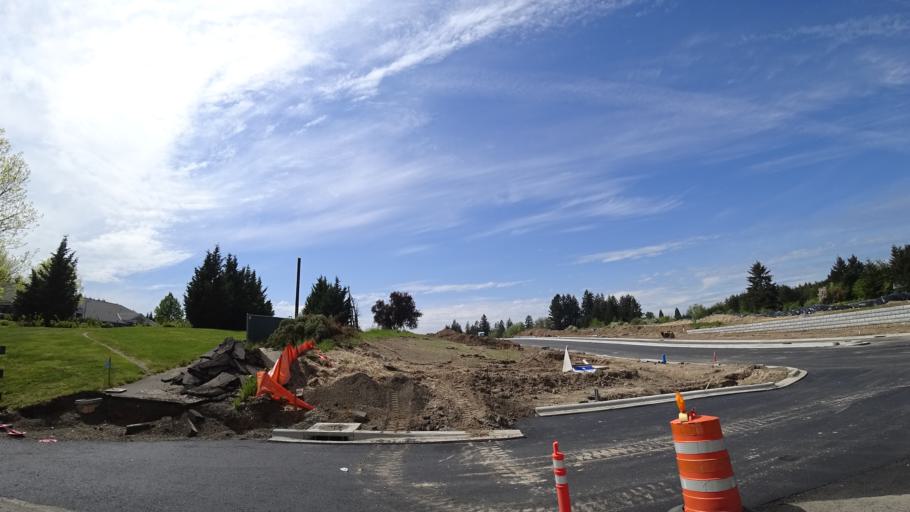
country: US
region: Oregon
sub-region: Washington County
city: Aloha
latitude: 45.4831
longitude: -122.8934
